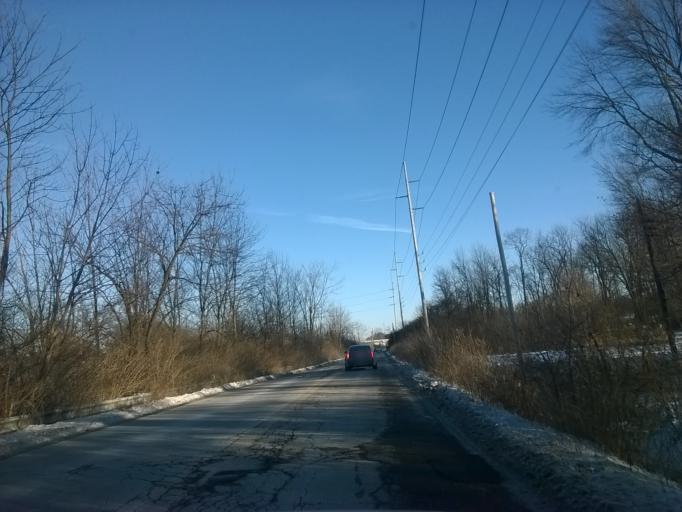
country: US
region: Indiana
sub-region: Marion County
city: Meridian Hills
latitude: 39.9268
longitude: -86.1328
